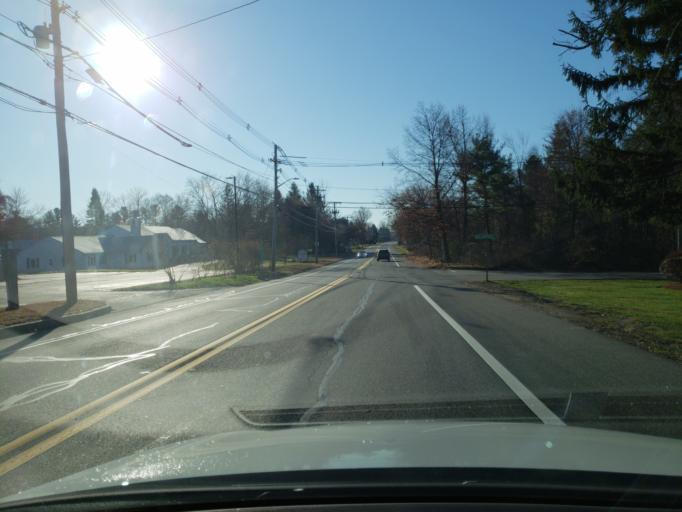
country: US
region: Massachusetts
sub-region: Essex County
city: Andover
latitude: 42.6277
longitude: -71.1269
